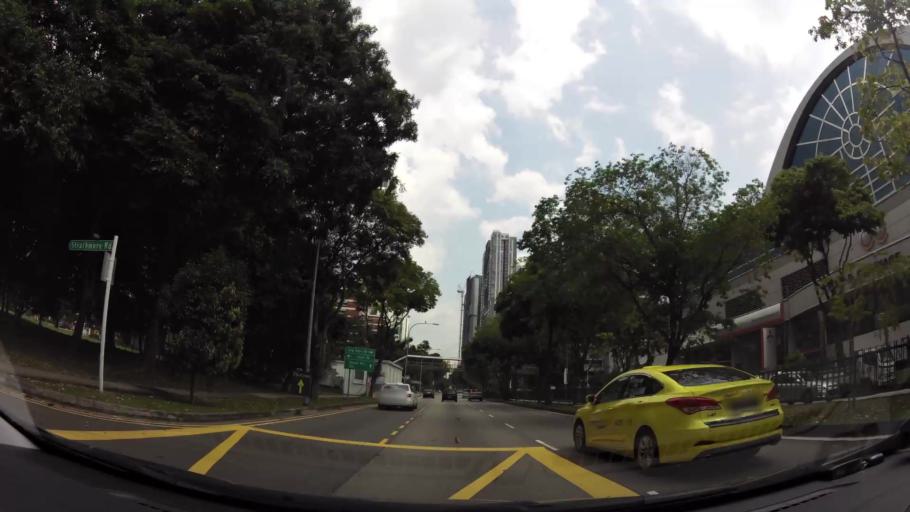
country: SG
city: Singapore
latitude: 1.2921
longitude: 103.8132
